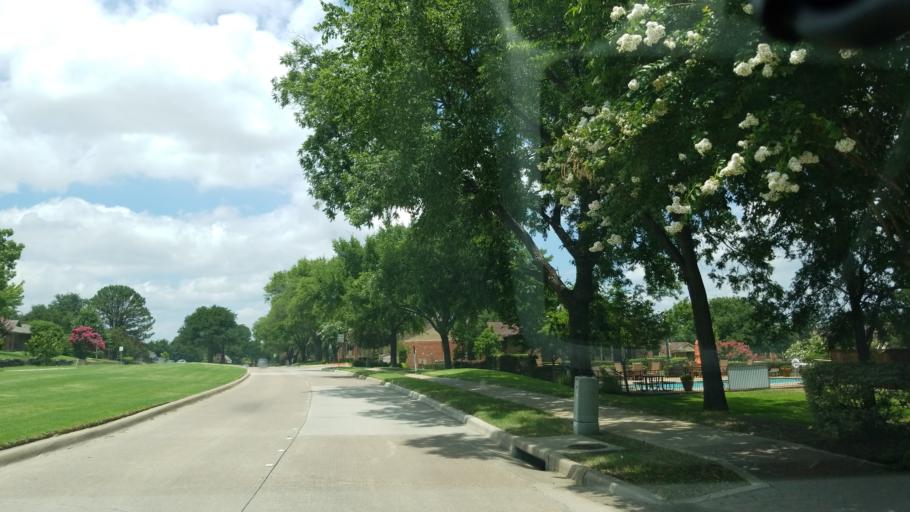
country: US
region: Texas
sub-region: Dallas County
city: Coppell
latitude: 32.9660
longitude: -96.9586
